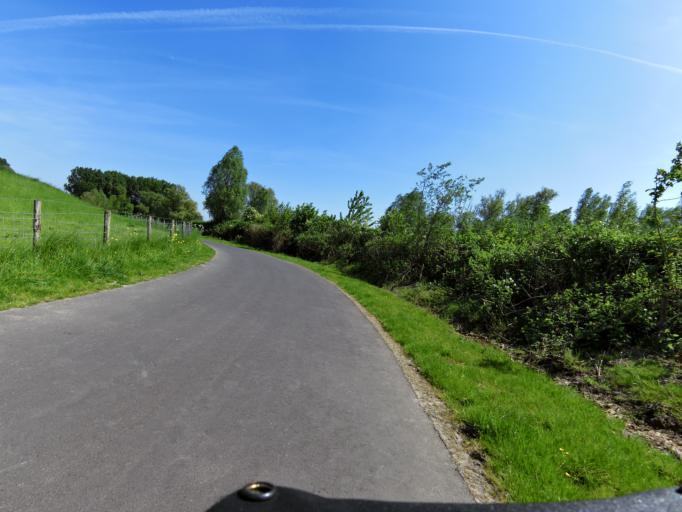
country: NL
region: South Holland
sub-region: Gemeente Barendrecht
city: Barendrecht
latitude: 51.8329
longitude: 4.5280
